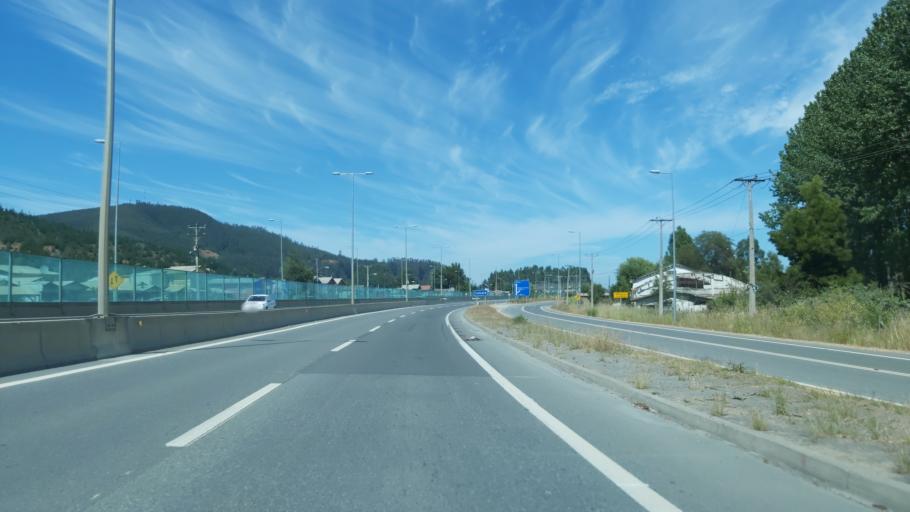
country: CL
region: Biobio
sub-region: Provincia de Concepcion
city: Lota
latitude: -37.1082
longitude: -73.1423
